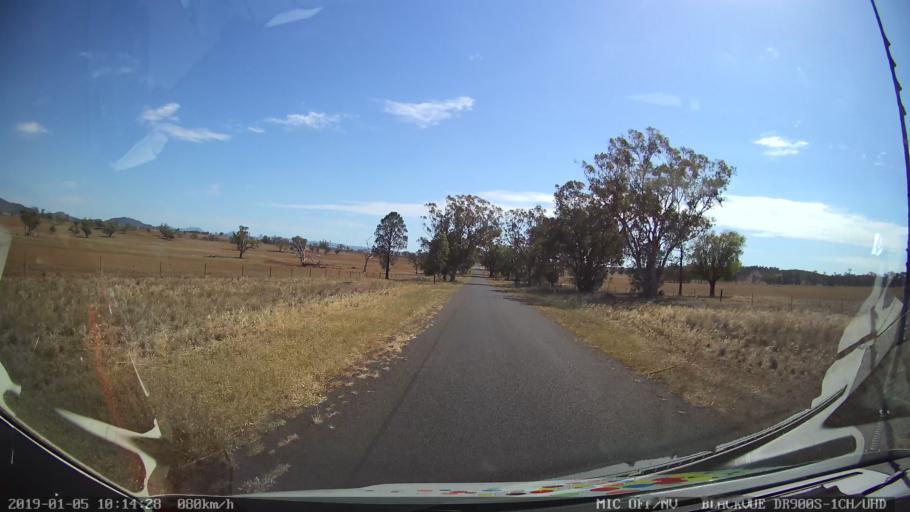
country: AU
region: New South Wales
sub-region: Gilgandra
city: Gilgandra
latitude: -31.5925
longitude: 148.9347
